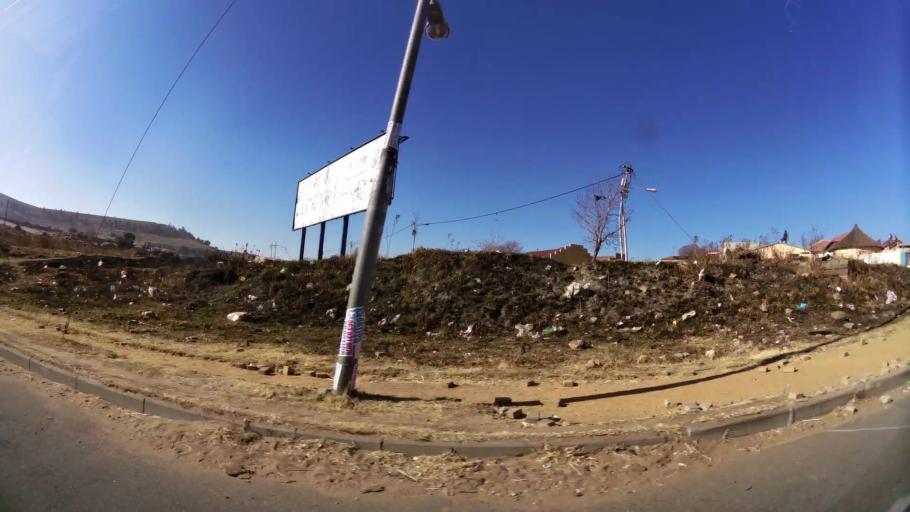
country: ZA
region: Gauteng
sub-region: City of Johannesburg Metropolitan Municipality
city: Soweto
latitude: -26.2256
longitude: 27.9376
